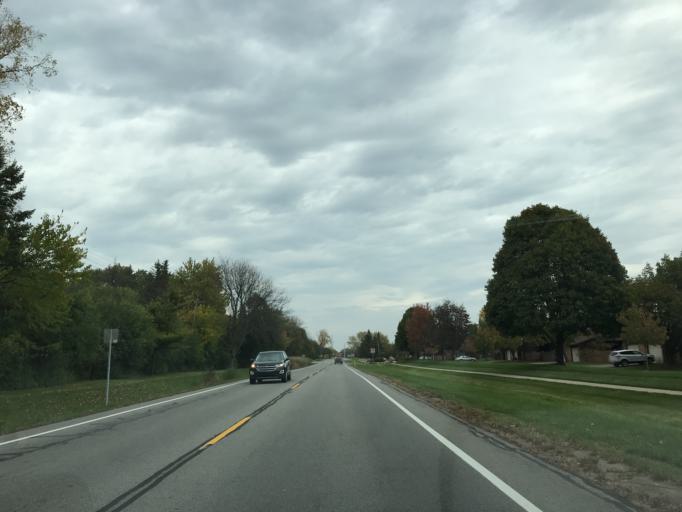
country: US
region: Michigan
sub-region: Oakland County
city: Franklin
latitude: 42.4798
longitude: -83.3186
